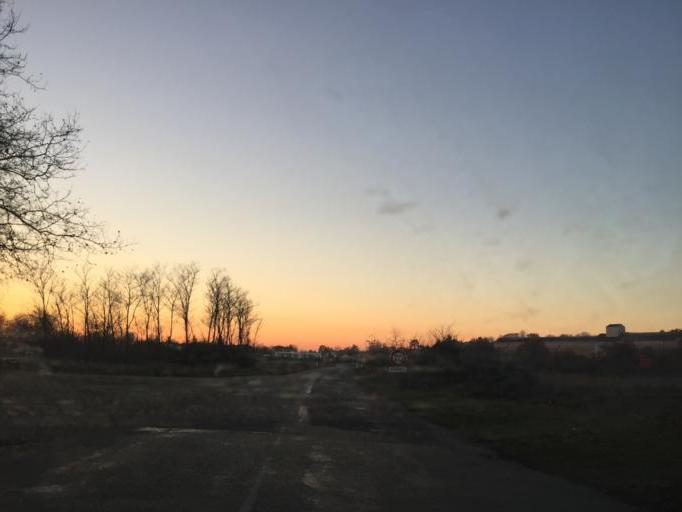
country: FR
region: Rhone-Alpes
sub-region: Departement de l'Ain
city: Beligneux
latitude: 45.8495
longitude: 5.1349
